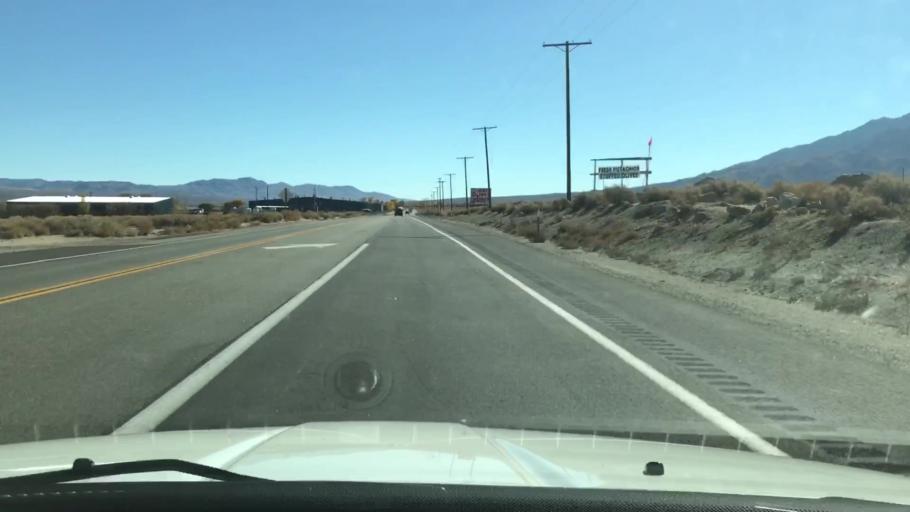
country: US
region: California
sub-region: Inyo County
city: Lone Pine
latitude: 36.3103
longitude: -118.0253
